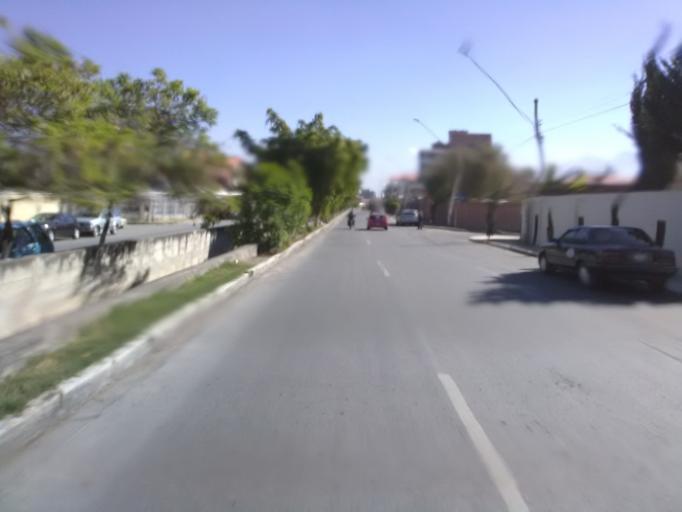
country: BO
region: Cochabamba
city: Cochabamba
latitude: -17.3826
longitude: -66.1871
